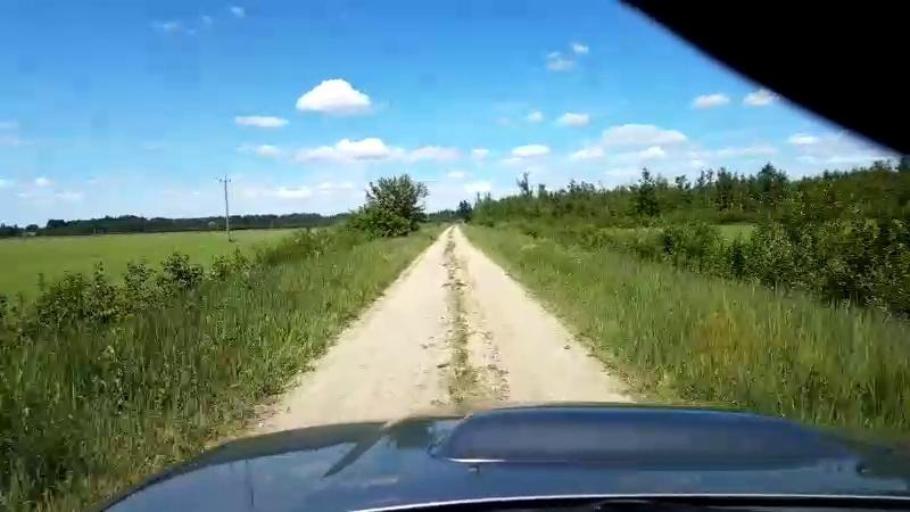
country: EE
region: Paernumaa
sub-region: Halinga vald
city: Parnu-Jaagupi
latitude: 58.5374
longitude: 24.5302
